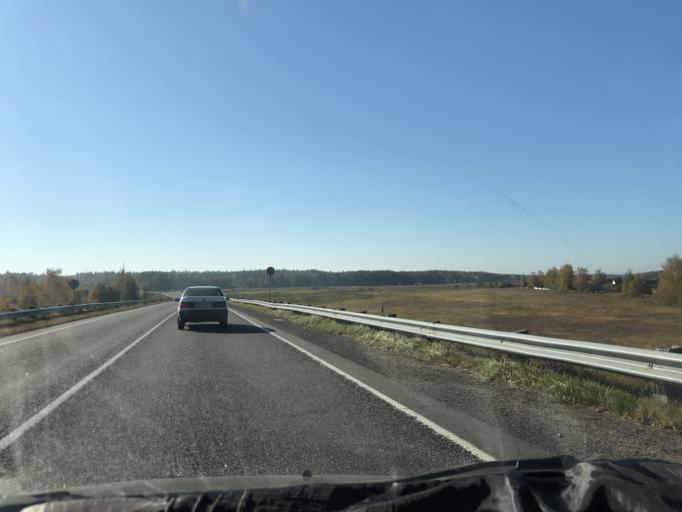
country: BY
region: Mogilev
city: Babruysk
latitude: 53.1788
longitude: 29.0461
